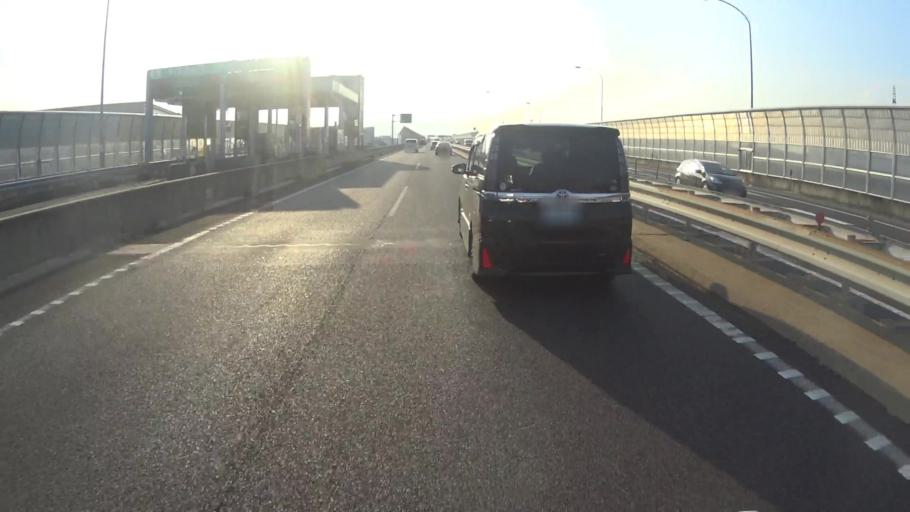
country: JP
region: Kyoto
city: Uji
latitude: 34.9058
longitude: 135.7894
